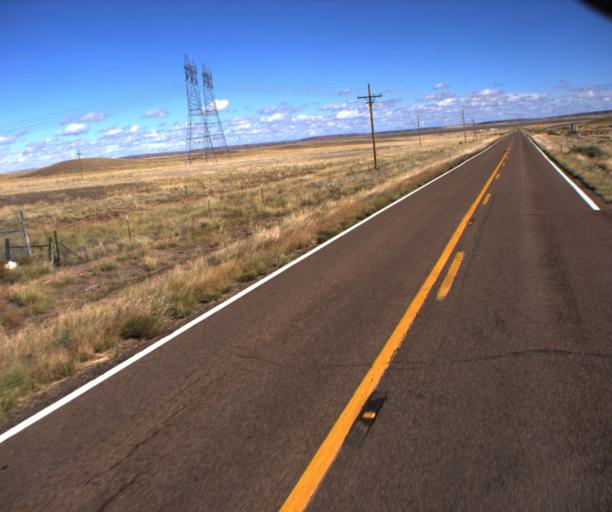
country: US
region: Arizona
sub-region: Apache County
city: Saint Johns
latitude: 34.5745
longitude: -109.3358
